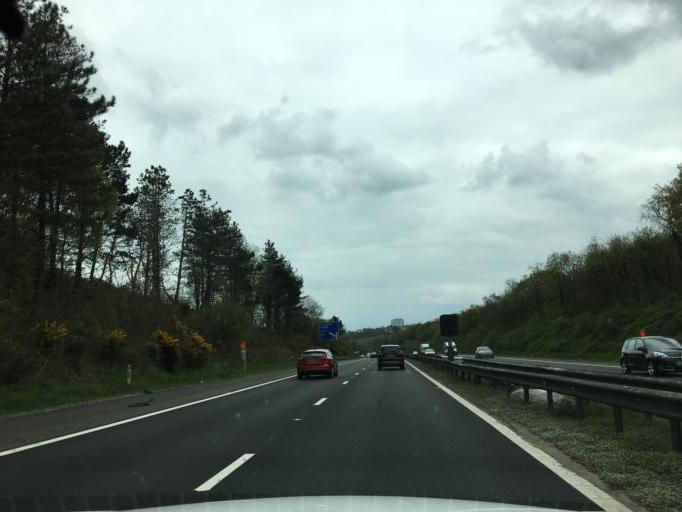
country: GB
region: Wales
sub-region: City and County of Swansea
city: Pontlliw
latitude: 51.6752
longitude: -3.9799
